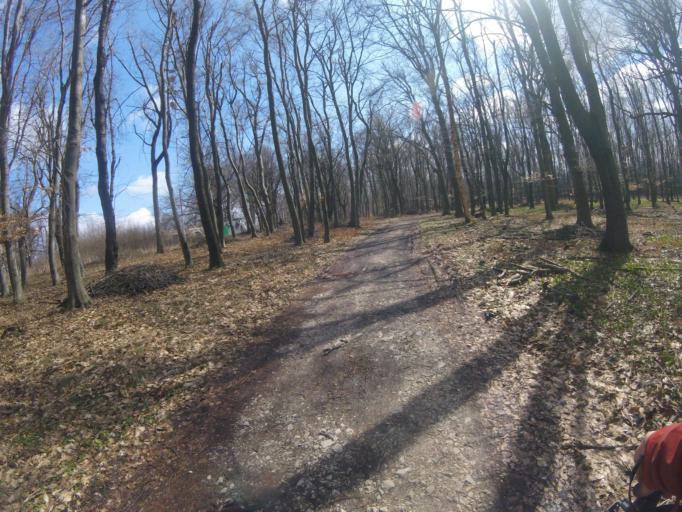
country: HU
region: Komarom-Esztergom
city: Tardos
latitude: 47.6795
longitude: 18.4875
